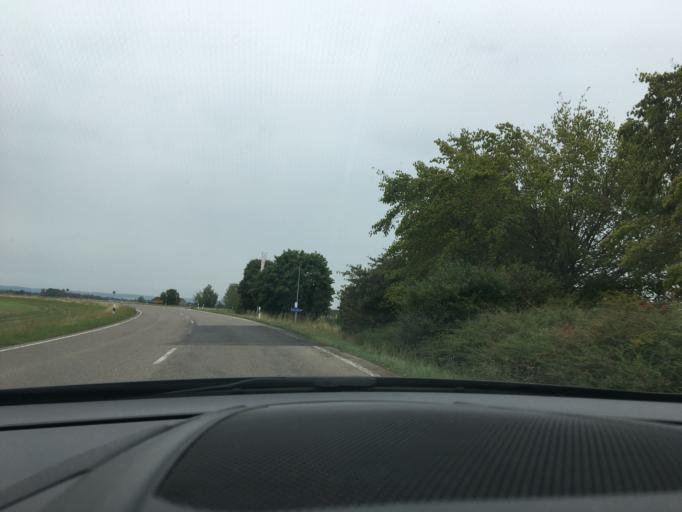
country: DE
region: Baden-Wuerttemberg
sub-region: Tuebingen Region
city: Erolzheim
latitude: 48.0882
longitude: 10.0799
